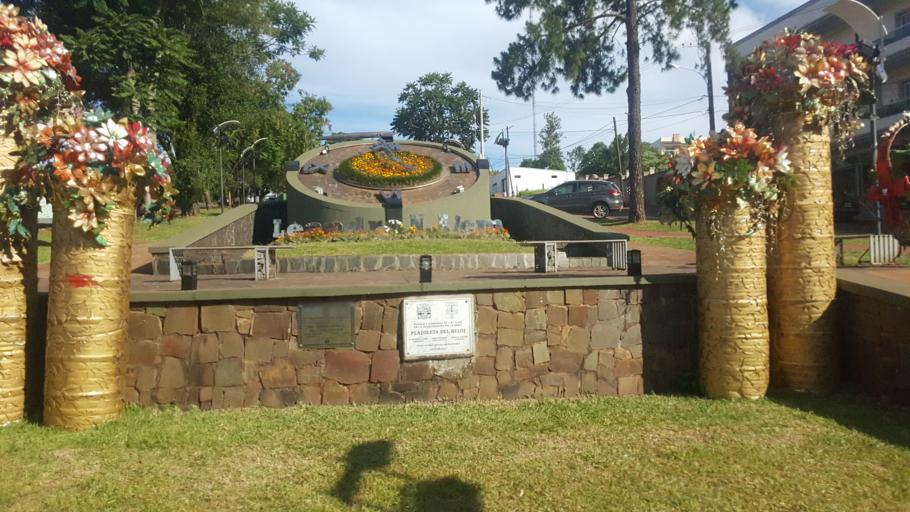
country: AR
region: Misiones
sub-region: Departamento de Leandro N. Alem
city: Leandro N. Alem
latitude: -27.6104
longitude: -55.3150
